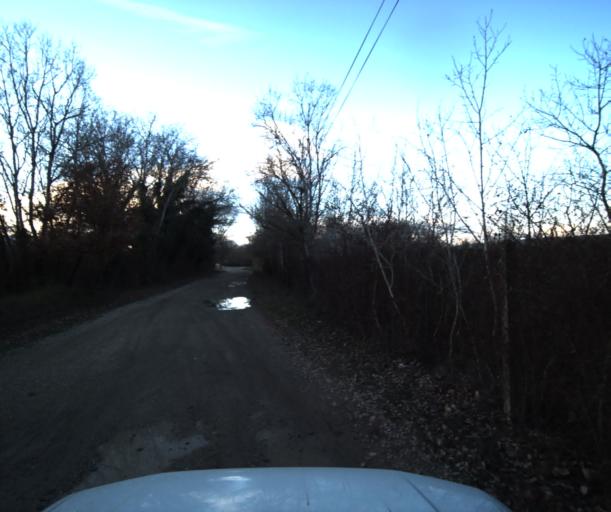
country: FR
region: Provence-Alpes-Cote d'Azur
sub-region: Departement du Vaucluse
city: Pertuis
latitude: 43.6689
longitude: 5.5024
